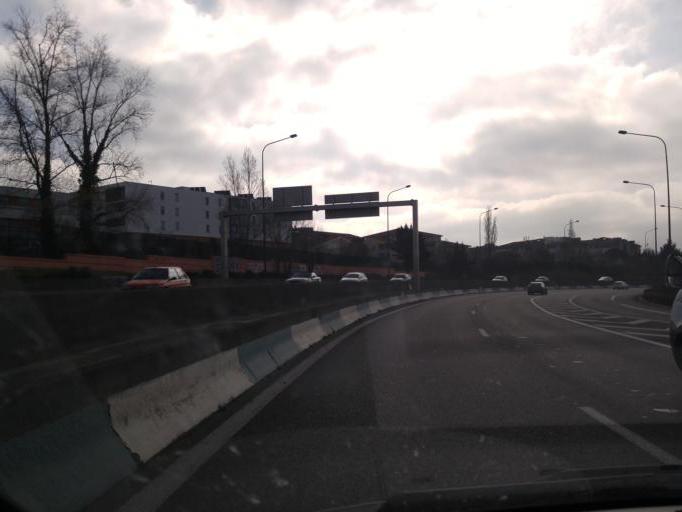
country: FR
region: Midi-Pyrenees
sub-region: Departement de la Haute-Garonne
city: Blagnac
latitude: 43.6181
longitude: 1.3940
